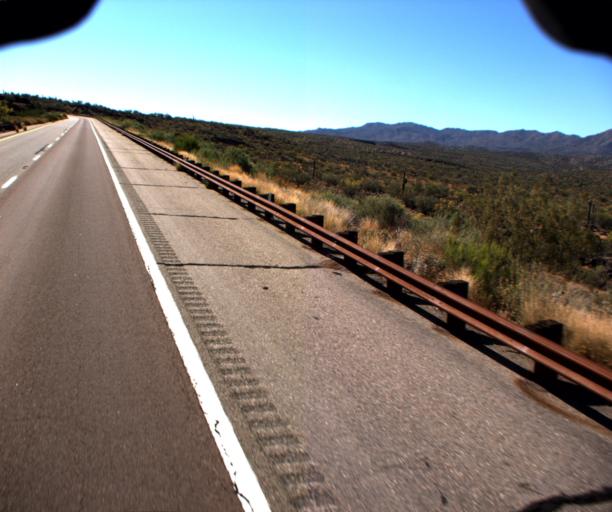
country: US
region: Arizona
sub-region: Yavapai County
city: Bagdad
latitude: 34.5048
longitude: -113.4101
